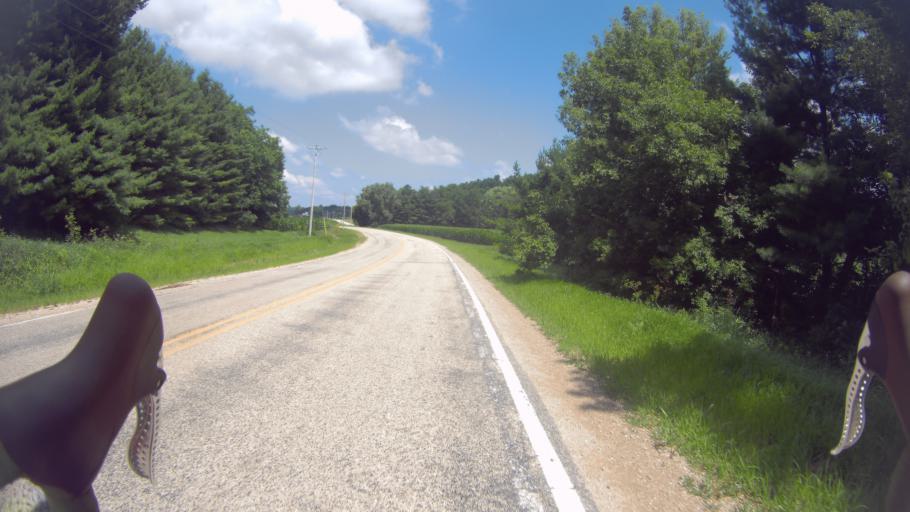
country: US
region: Wisconsin
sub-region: Columbia County
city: Lodi
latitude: 43.2470
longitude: -89.6059
